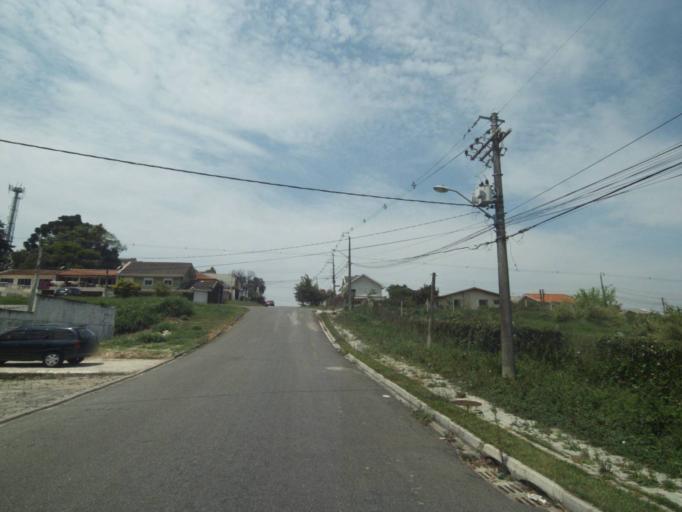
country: BR
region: Parana
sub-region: Pinhais
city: Pinhais
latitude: -25.4183
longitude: -49.2101
